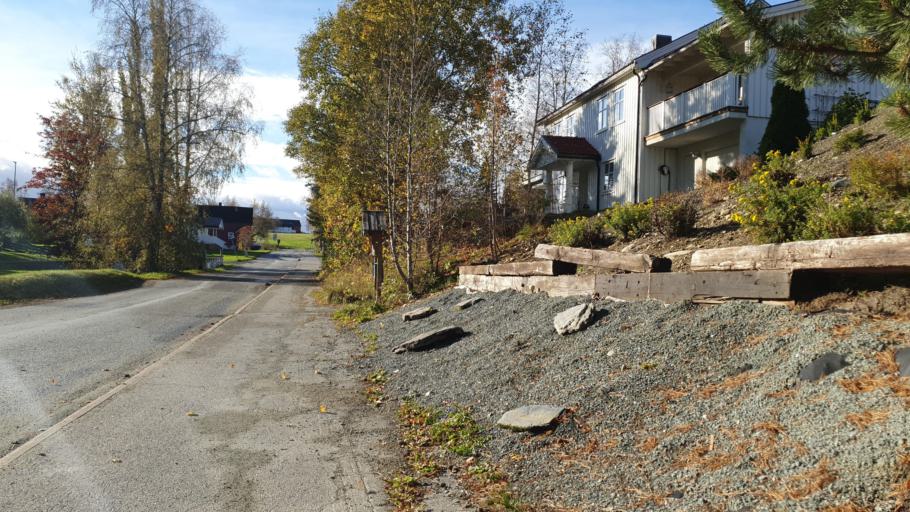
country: NO
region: Sor-Trondelag
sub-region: Klaebu
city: Klaebu
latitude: 63.3000
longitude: 10.4771
